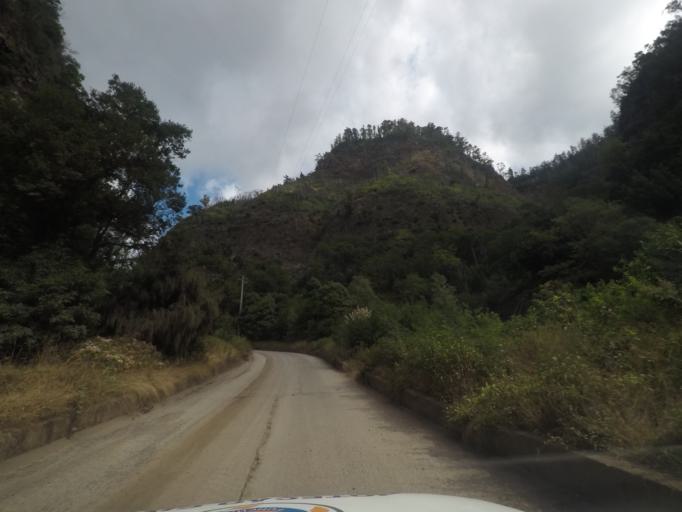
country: PT
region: Madeira
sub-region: Funchal
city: Nossa Senhora do Monte
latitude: 32.6864
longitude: -16.9152
